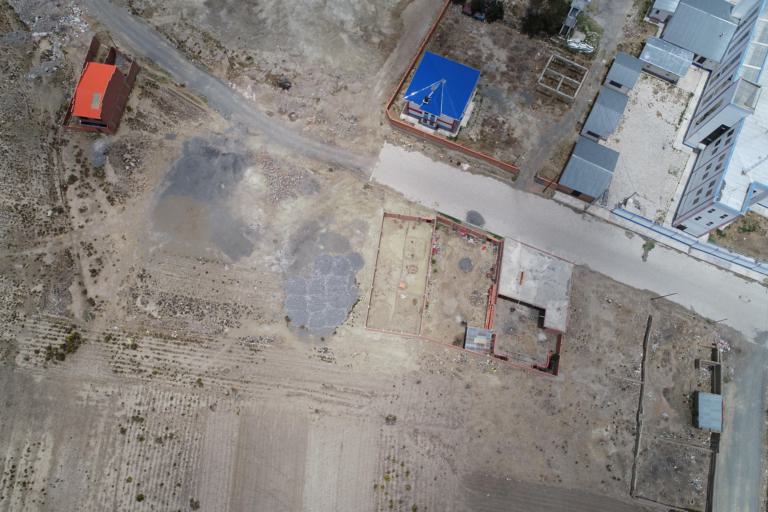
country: BO
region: La Paz
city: Achacachi
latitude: -16.0436
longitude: -68.6930
